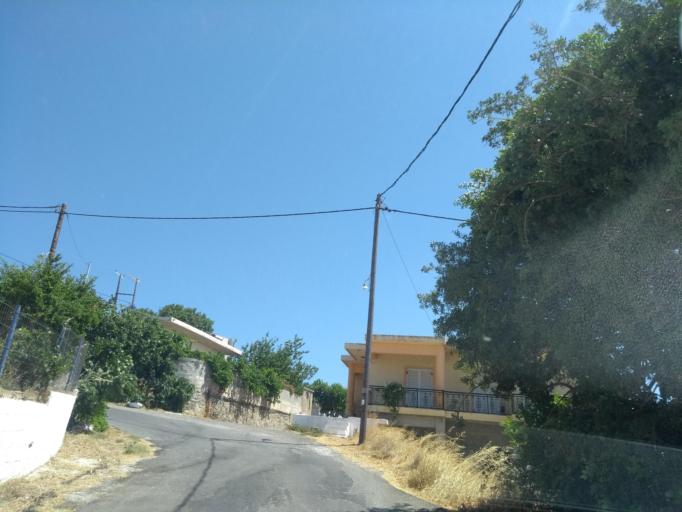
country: GR
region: Crete
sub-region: Nomos Chanias
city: Vryses
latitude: 35.3610
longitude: 23.5340
